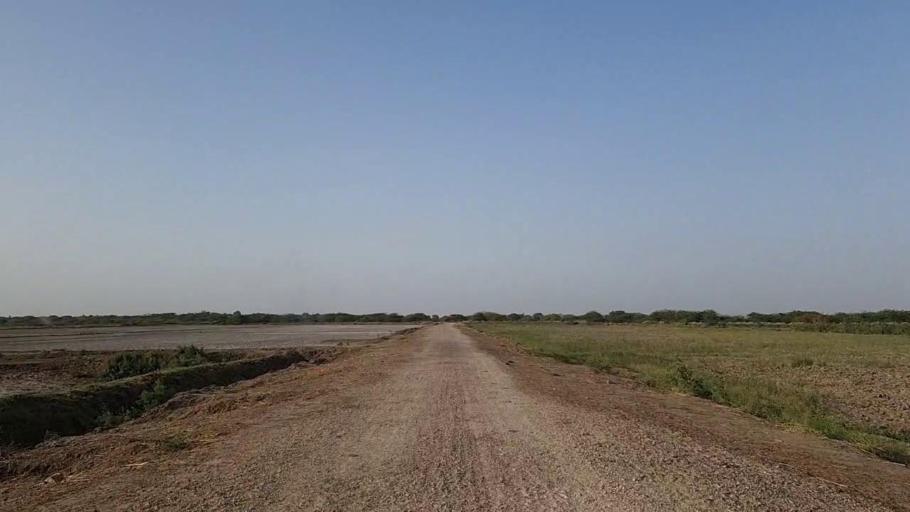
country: PK
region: Sindh
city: Jati
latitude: 24.3806
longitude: 68.1481
